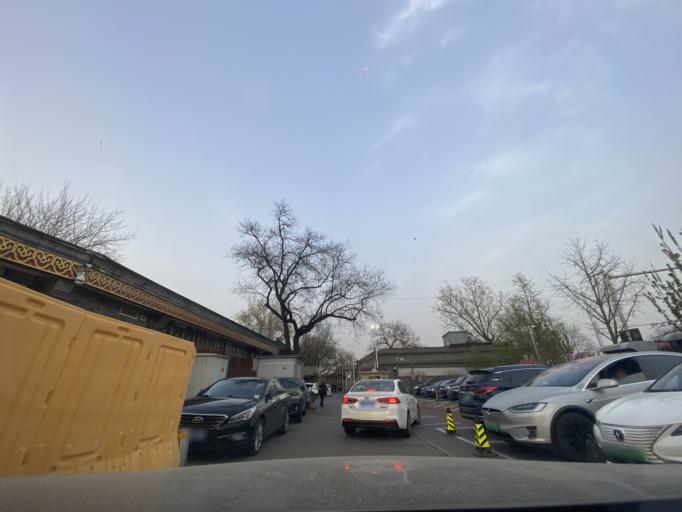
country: CN
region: Beijing
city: Jingshan
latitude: 39.9323
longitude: 116.3871
